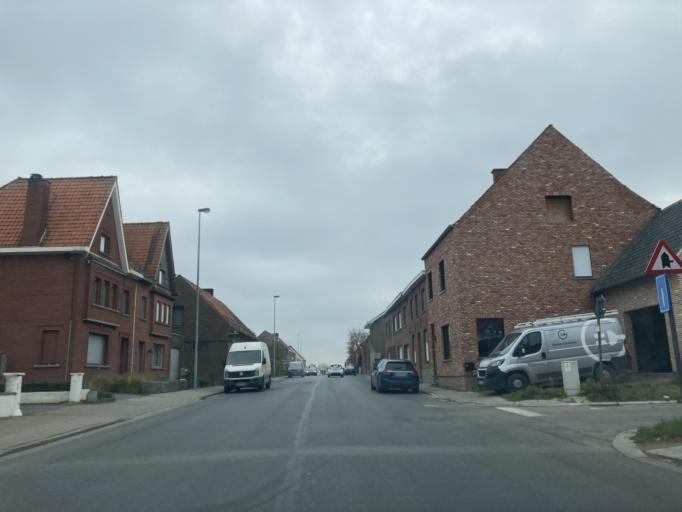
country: BE
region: Flanders
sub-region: Provincie West-Vlaanderen
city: Izegem
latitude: 50.8685
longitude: 3.1842
